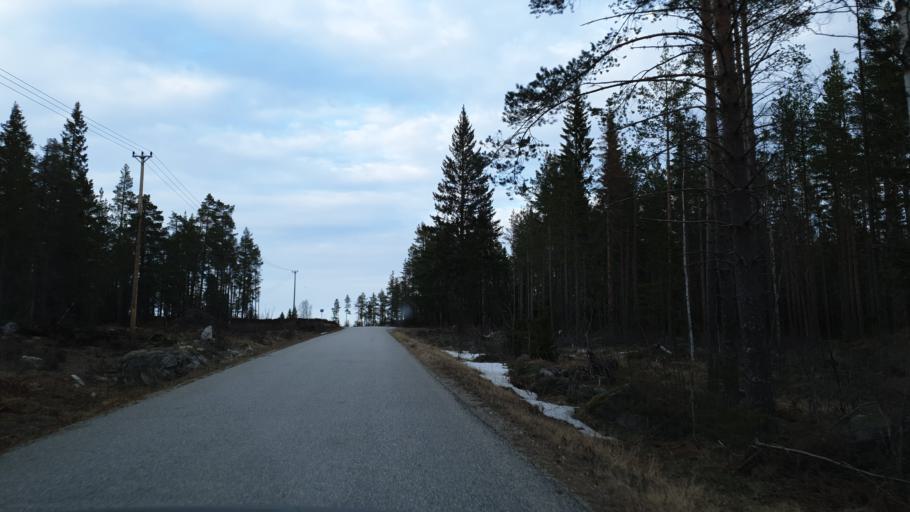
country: SE
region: Vaesternorrland
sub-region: Sundsvalls Kommun
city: Njurundabommen
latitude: 62.0104
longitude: 17.3981
